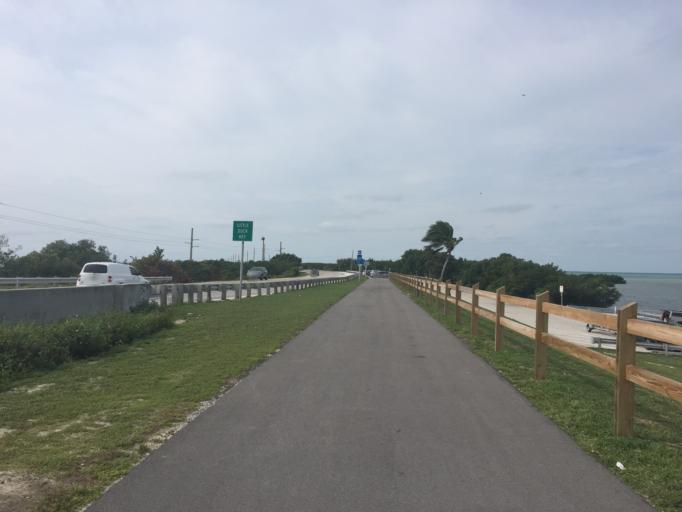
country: US
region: Florida
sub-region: Monroe County
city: Big Pine Key
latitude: 24.6824
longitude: -81.2285
